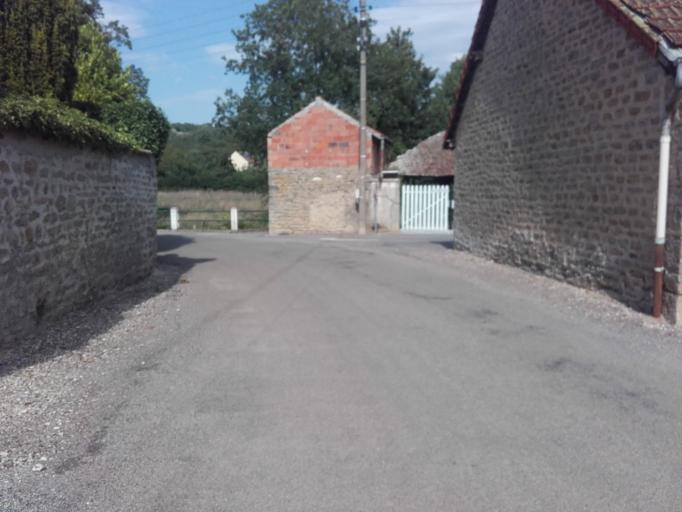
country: FR
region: Bourgogne
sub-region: Departement de la Cote-d'Or
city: Nolay
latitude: 46.9159
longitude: 4.6344
